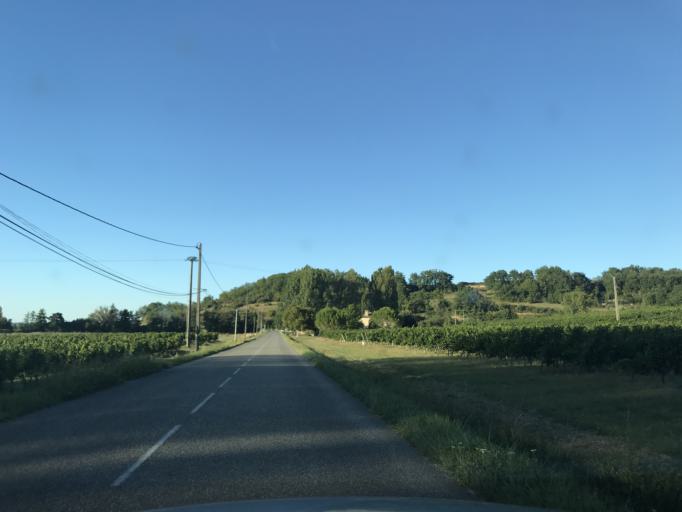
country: FR
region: Aquitaine
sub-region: Departement de la Gironde
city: Mouliets-et-Villemartin
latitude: 44.7925
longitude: -0.0448
